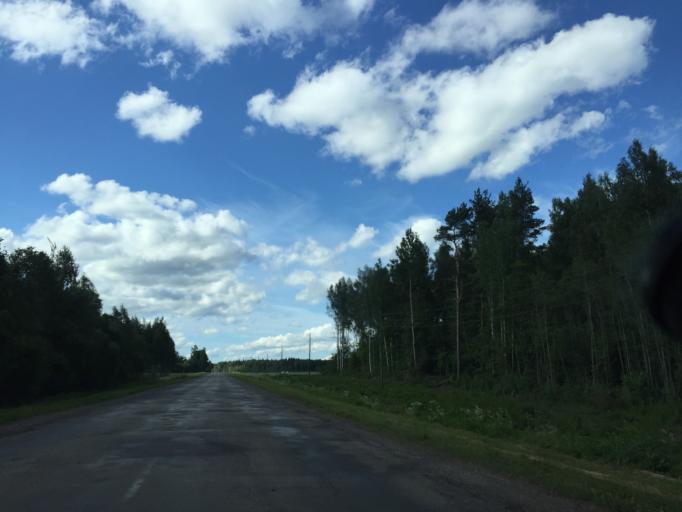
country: LV
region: Vecumnieki
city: Vecumnieki
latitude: 56.4232
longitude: 24.6238
